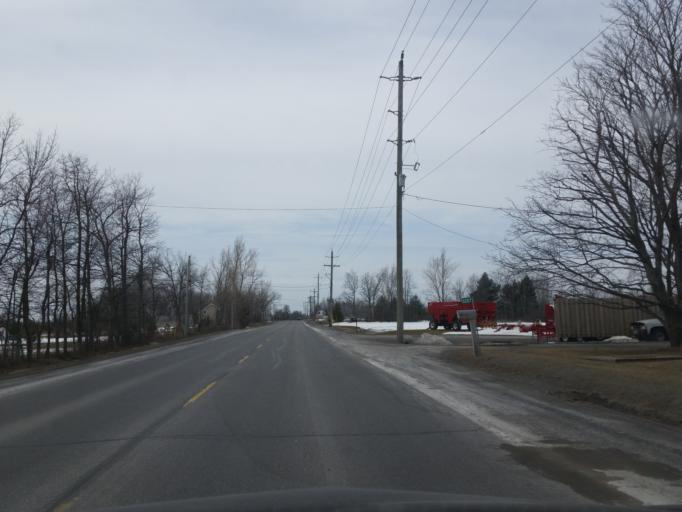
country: CA
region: Ontario
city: Skatepark
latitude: 44.2556
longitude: -76.7863
